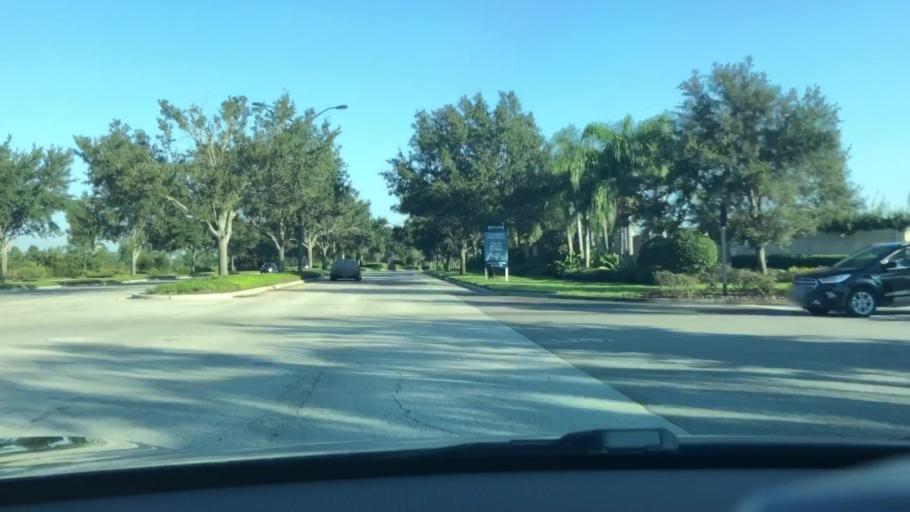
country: US
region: Florida
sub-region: Orange County
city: Meadow Woods
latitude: 28.3897
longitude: -81.2760
